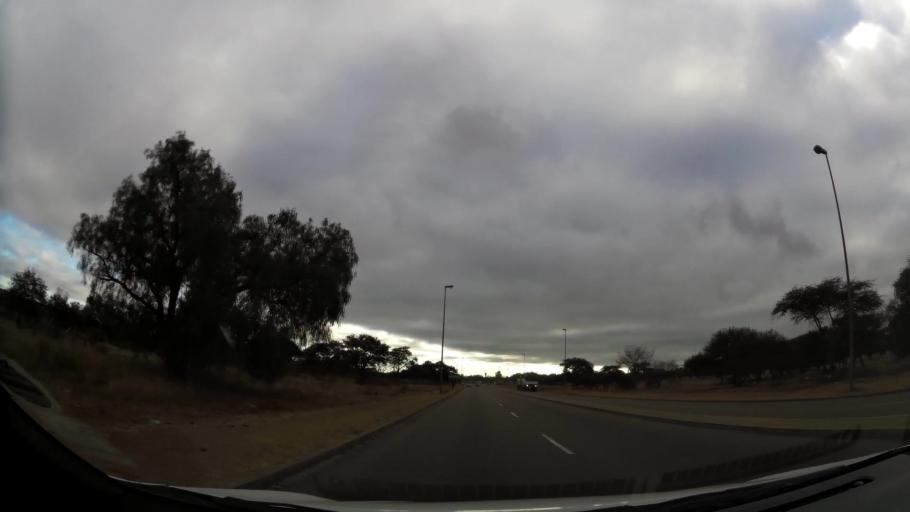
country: ZA
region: Limpopo
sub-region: Capricorn District Municipality
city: Polokwane
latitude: -23.8850
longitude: 29.4313
